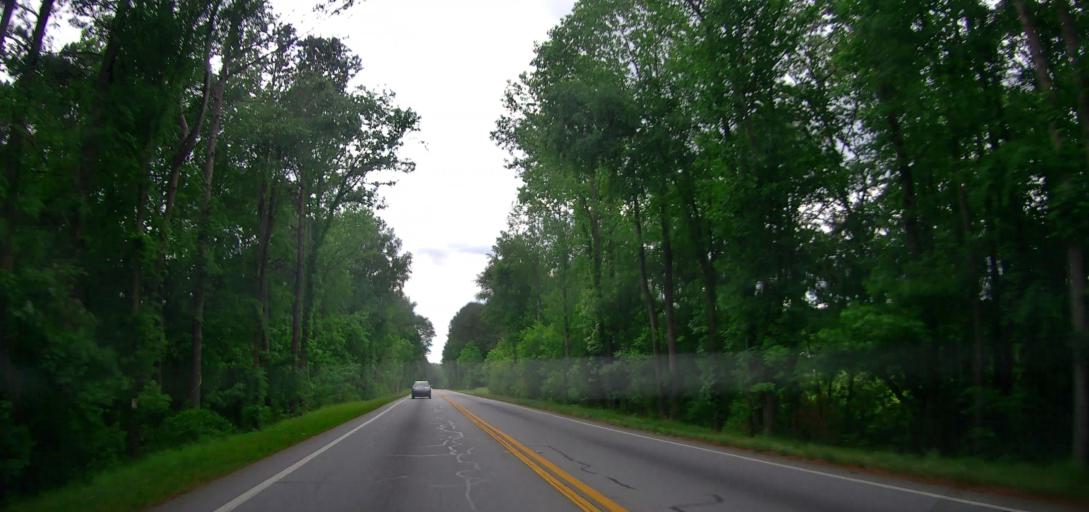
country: US
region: Georgia
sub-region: Walton County
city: Walnut Grove
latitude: 33.7240
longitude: -83.9101
